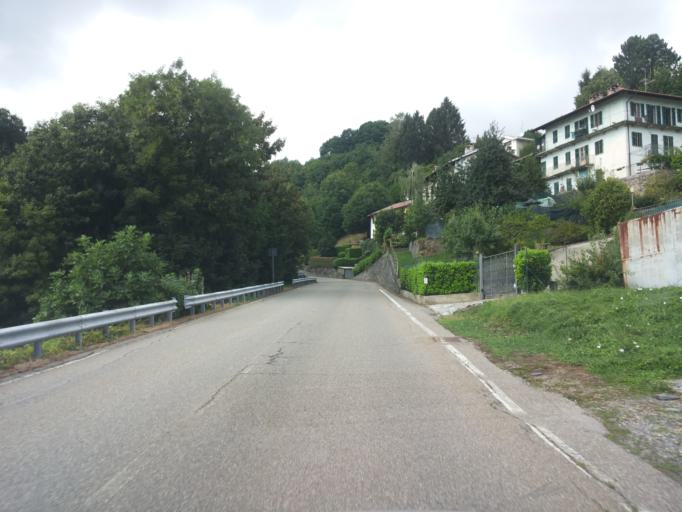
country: IT
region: Piedmont
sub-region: Provincia di Biella
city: Pollone
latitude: 45.5964
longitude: 8.0078
